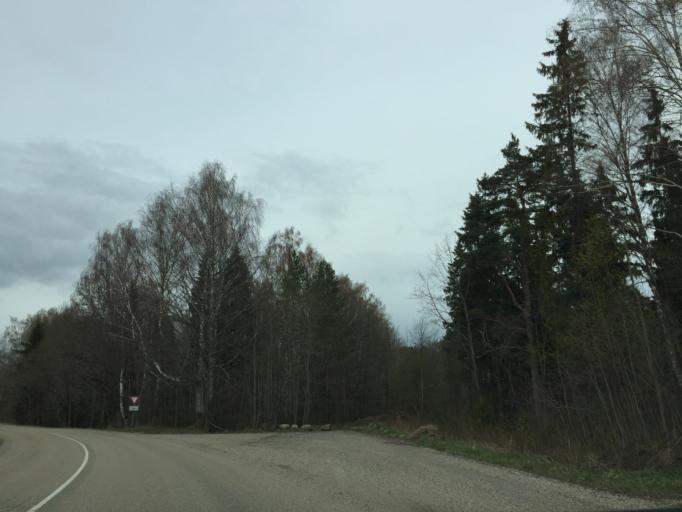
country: LV
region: Amatas Novads
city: Drabesi
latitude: 57.2600
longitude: 25.2717
